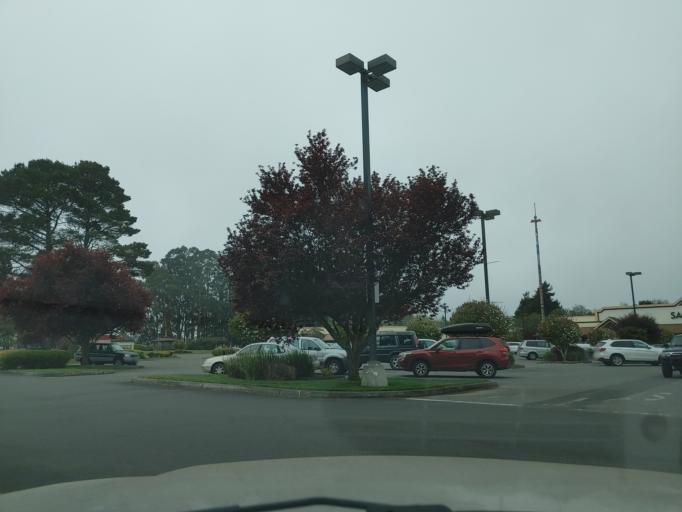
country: US
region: California
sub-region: Humboldt County
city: McKinleyville
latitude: 40.9437
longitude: -124.1015
